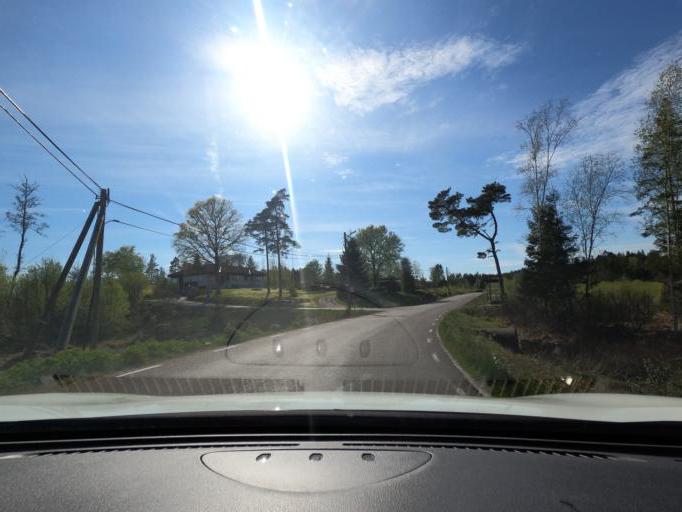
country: SE
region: Vaestra Goetaland
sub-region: Harryda Kommun
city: Landvetter
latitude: 57.6186
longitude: 12.3097
